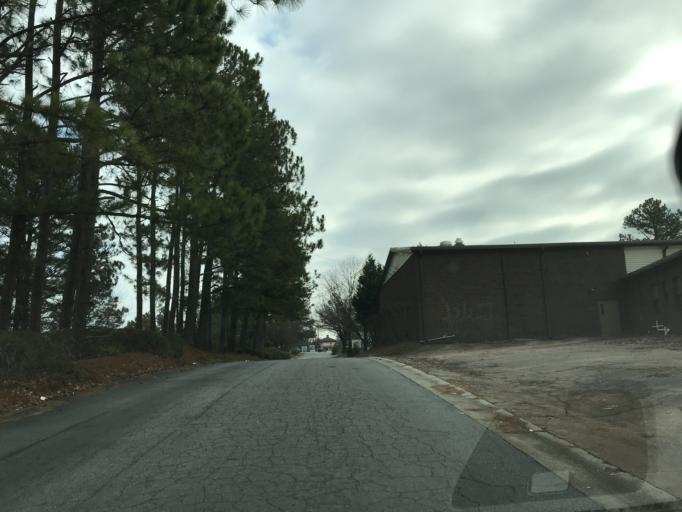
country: US
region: Georgia
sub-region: Clayton County
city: Morrow
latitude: 33.5658
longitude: -84.3736
